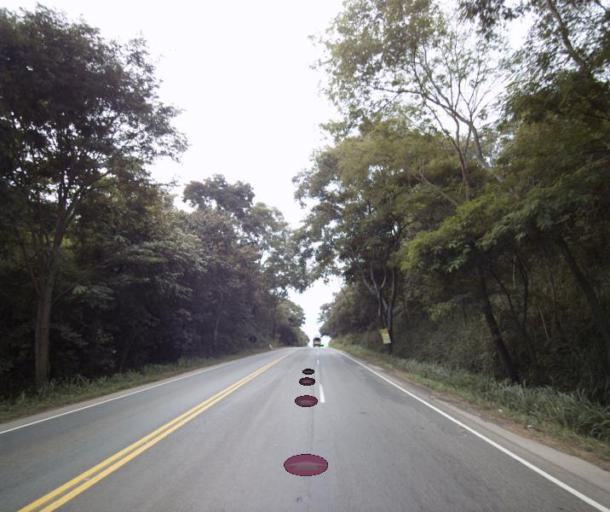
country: BR
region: Goias
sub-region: Rialma
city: Rialma
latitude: -15.2440
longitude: -49.5572
